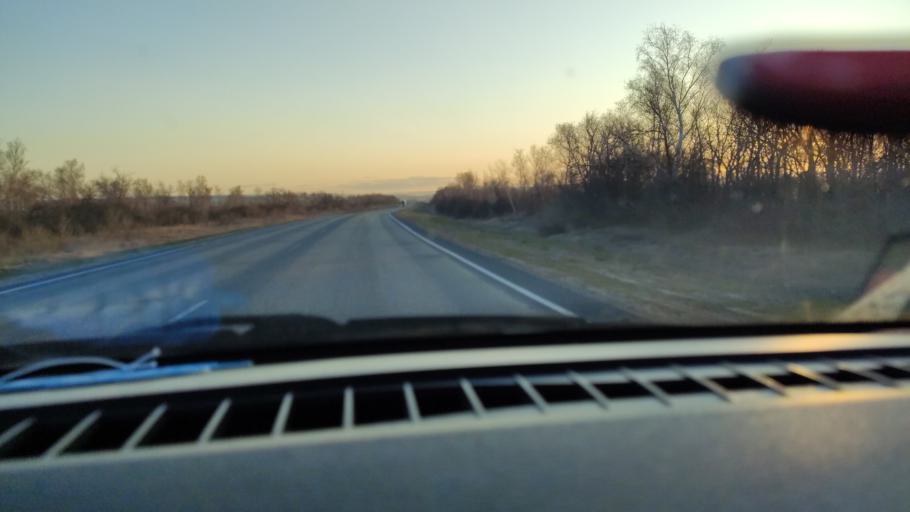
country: RU
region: Saratov
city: Sinodskoye
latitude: 51.9545
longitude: 46.6131
